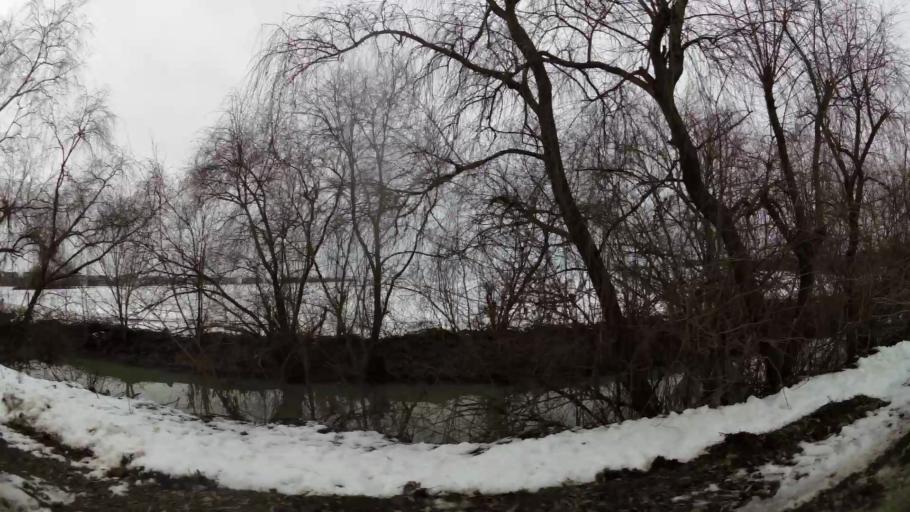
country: RO
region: Ilfov
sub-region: Comuna Tunari
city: Tunari
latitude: 44.5509
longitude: 26.1293
